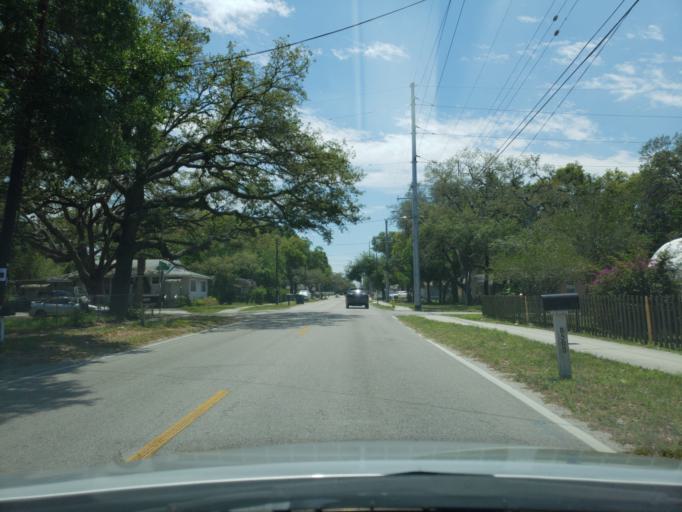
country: US
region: Florida
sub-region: Hillsborough County
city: Carrollwood
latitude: 28.0275
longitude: -82.4677
